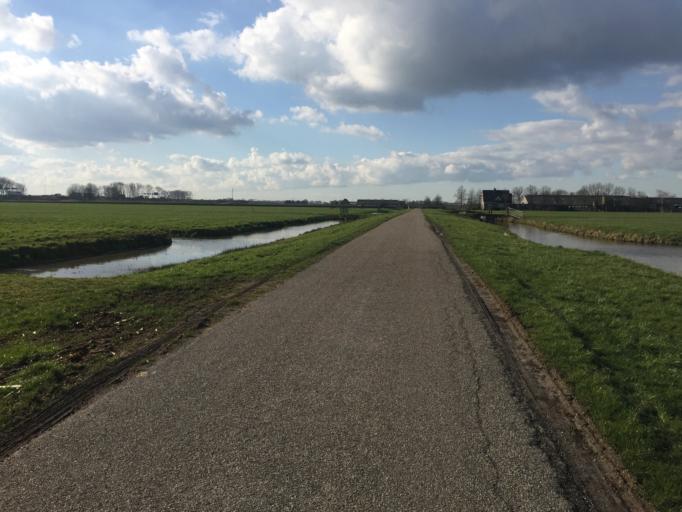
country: NL
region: South Holland
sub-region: Bodegraven-Reeuwijk
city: Bodegraven
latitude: 52.0668
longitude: 4.8139
